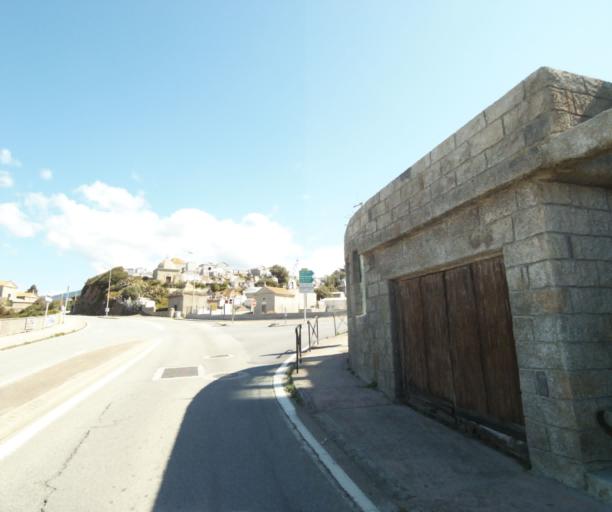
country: FR
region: Corsica
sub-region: Departement de la Corse-du-Sud
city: Propriano
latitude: 41.6782
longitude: 8.9108
